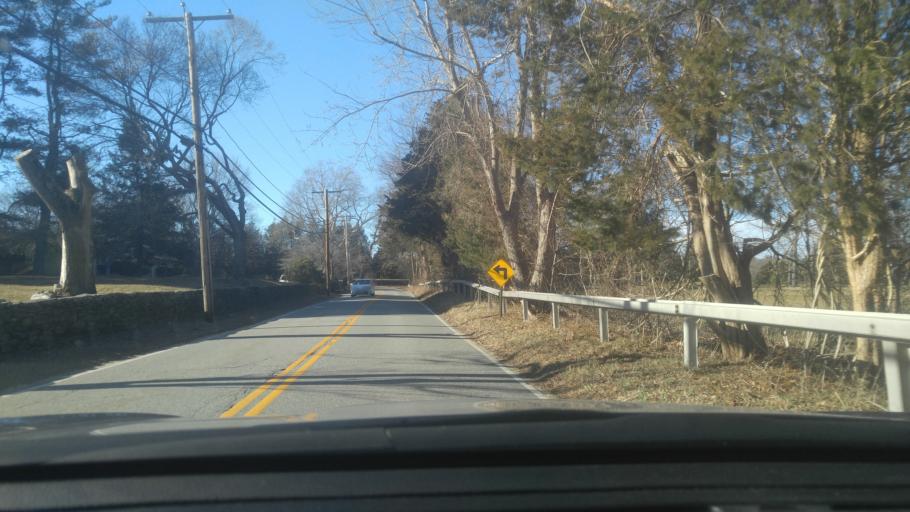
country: US
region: Rhode Island
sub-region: Kent County
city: East Greenwich
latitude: 41.6401
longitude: -71.4193
